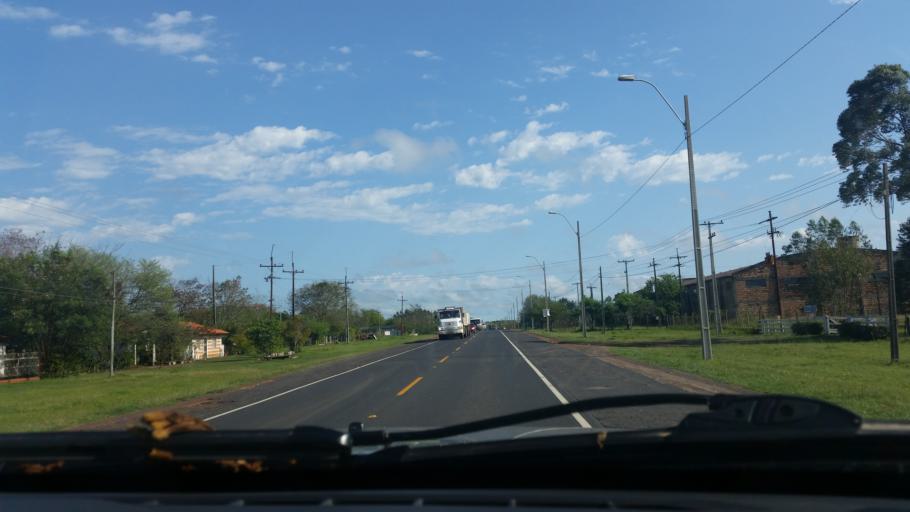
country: PY
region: Presidente Hayes
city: Villa Hayes
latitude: -25.0512
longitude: -57.5399
